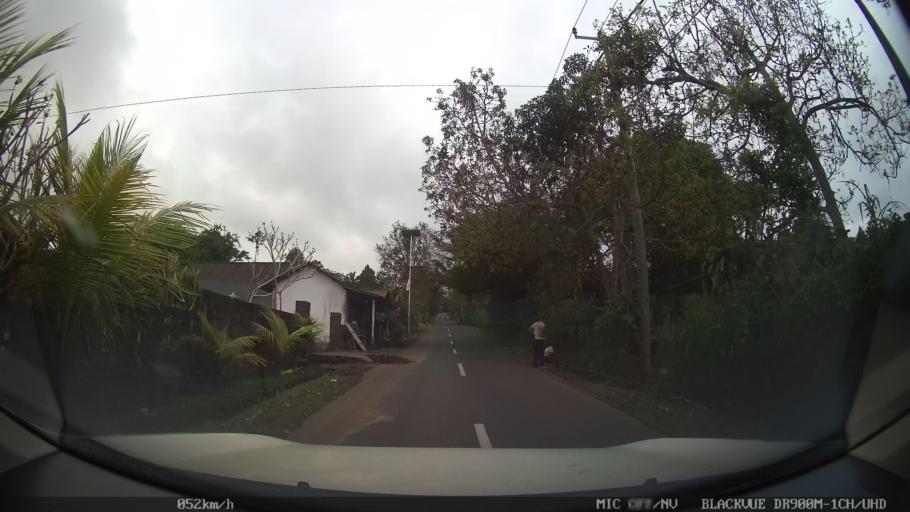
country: ID
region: Bali
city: Banjar Geriana Kangin
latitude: -8.3882
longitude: 115.4448
